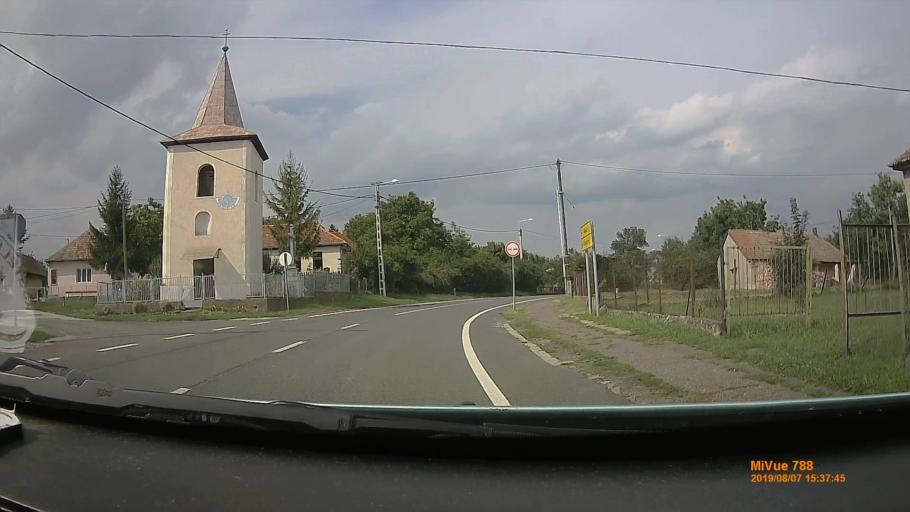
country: HU
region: Borsod-Abauj-Zemplen
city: Encs
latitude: 48.4204
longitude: 21.1749
